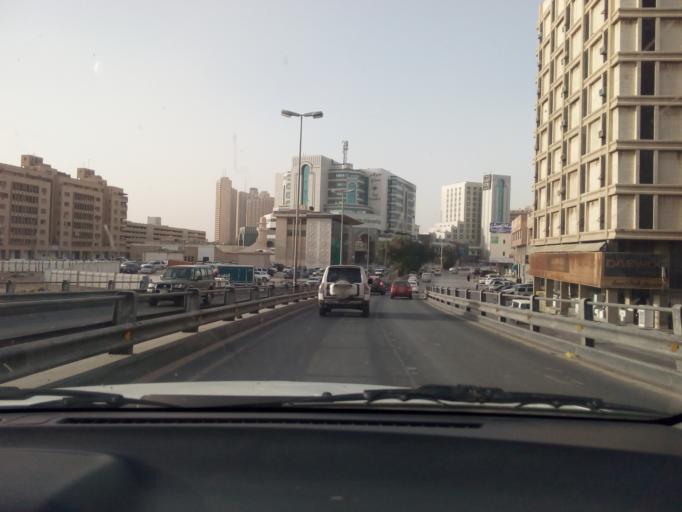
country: SA
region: Ar Riyad
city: Riyadh
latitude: 24.6307
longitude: 46.7168
